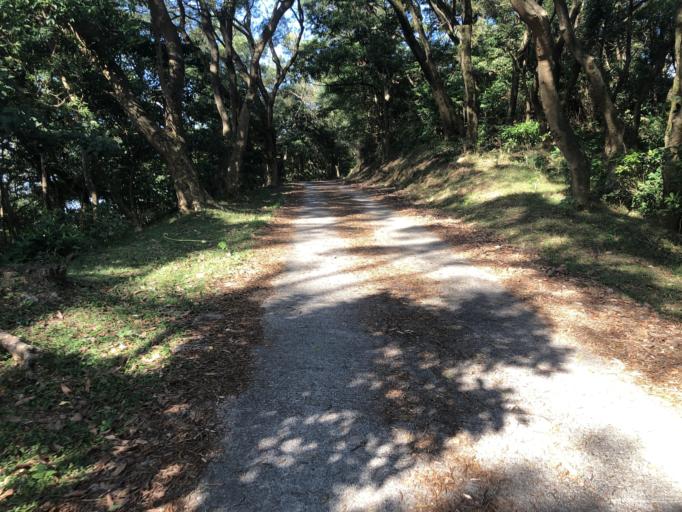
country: HK
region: Tsuen Wan
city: Tsuen Wan
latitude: 22.3936
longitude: 114.0862
